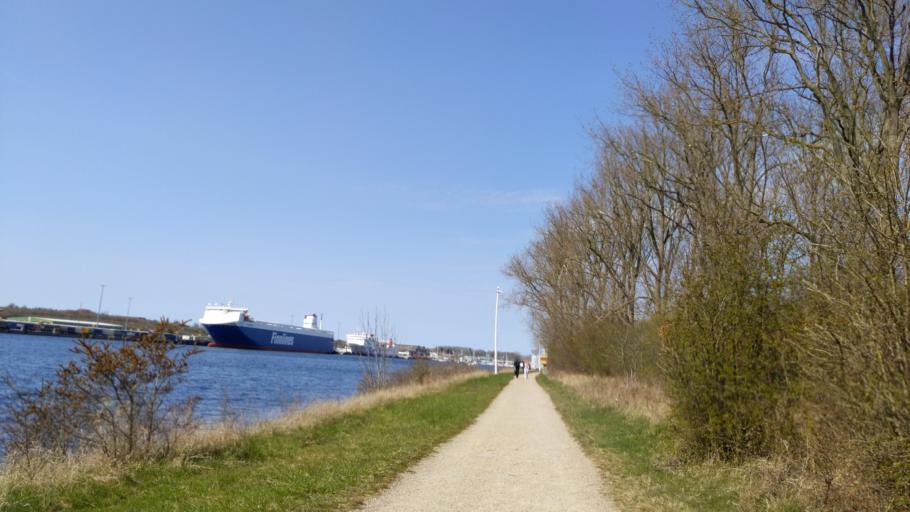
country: DE
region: Schleswig-Holstein
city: Travemuende
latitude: 53.9428
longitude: 10.8652
